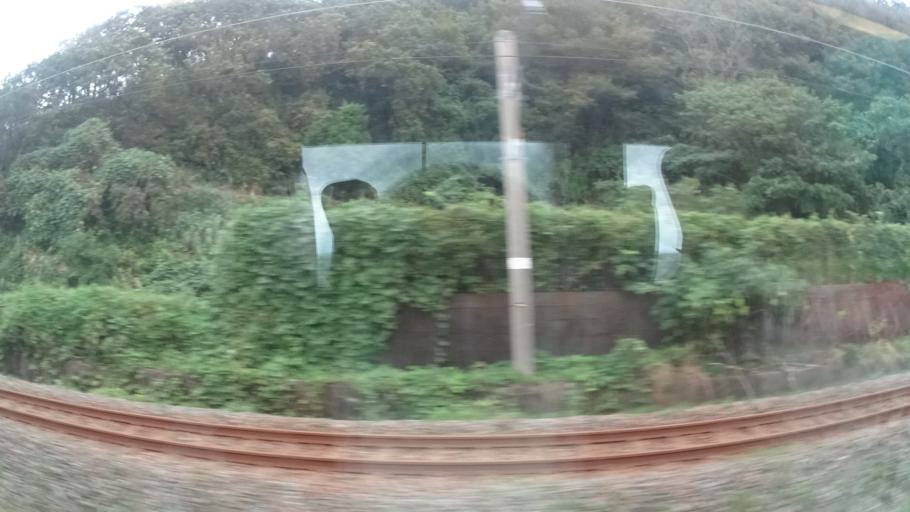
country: JP
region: Yamagata
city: Tsuruoka
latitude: 38.5780
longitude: 139.5595
